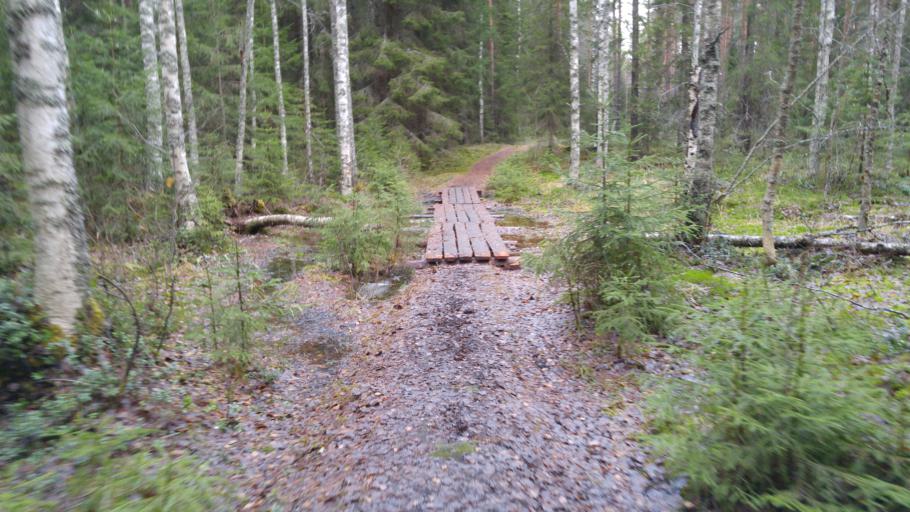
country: FI
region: Pirkanmaa
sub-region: Tampere
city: Kangasala
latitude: 61.6041
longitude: 23.9895
